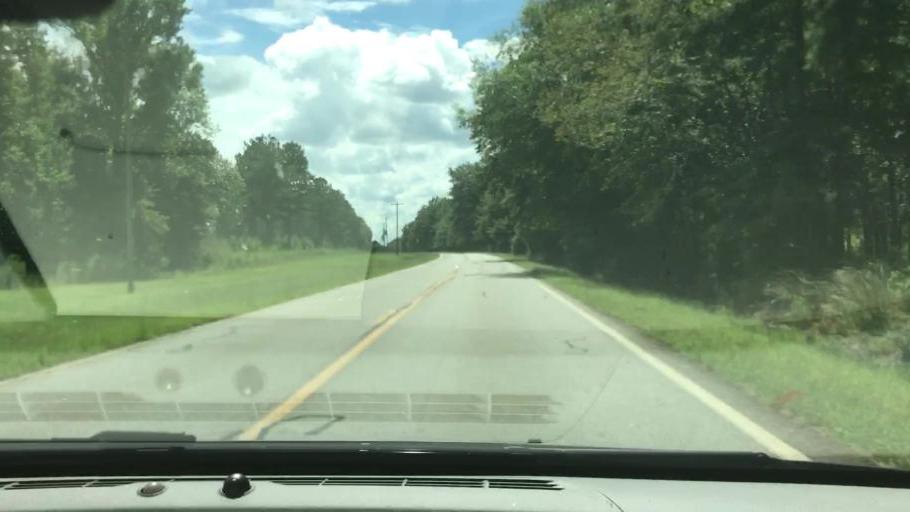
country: US
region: Georgia
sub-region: Quitman County
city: Georgetown
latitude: 32.1137
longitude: -85.0376
